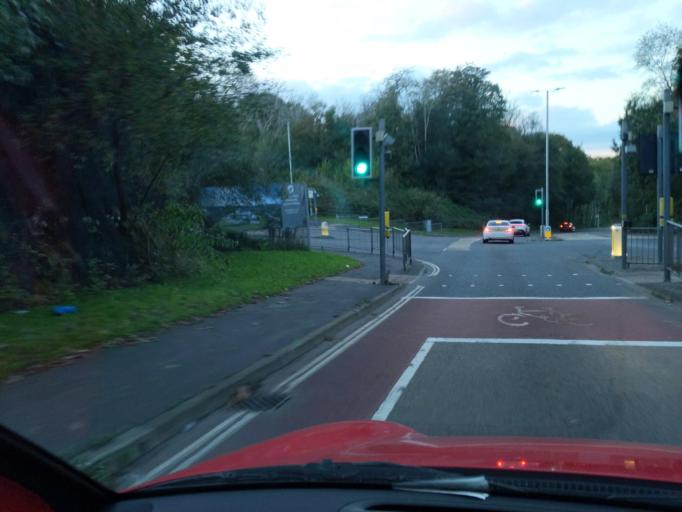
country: GB
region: England
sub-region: Plymouth
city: Plymouth
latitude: 50.4178
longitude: -4.1370
